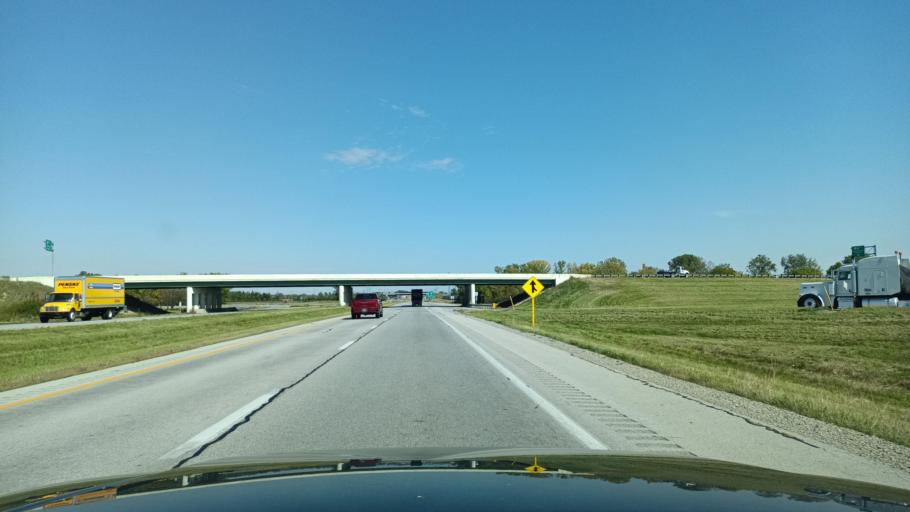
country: US
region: Ohio
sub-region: Henry County
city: Napoleon
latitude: 41.3954
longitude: -84.1493
